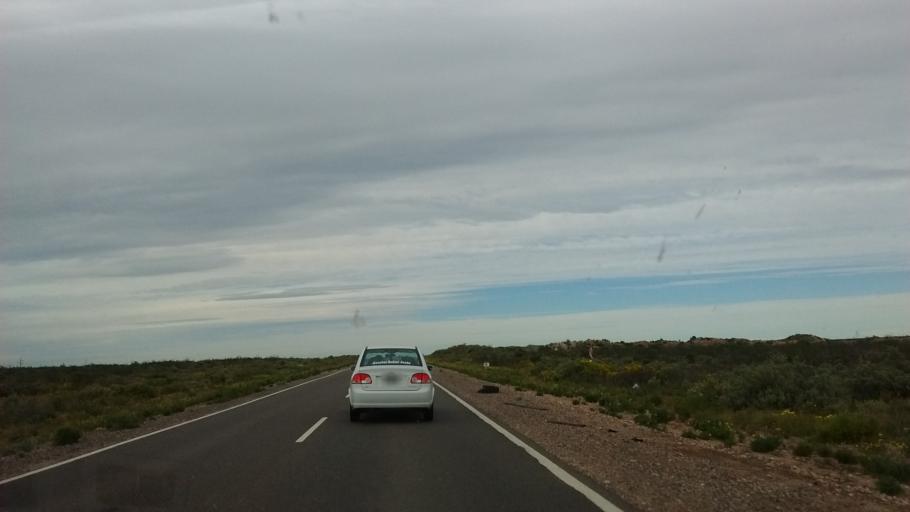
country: AR
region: Rio Negro
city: Contraalmirante Cordero
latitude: -38.3458
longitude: -68.0129
